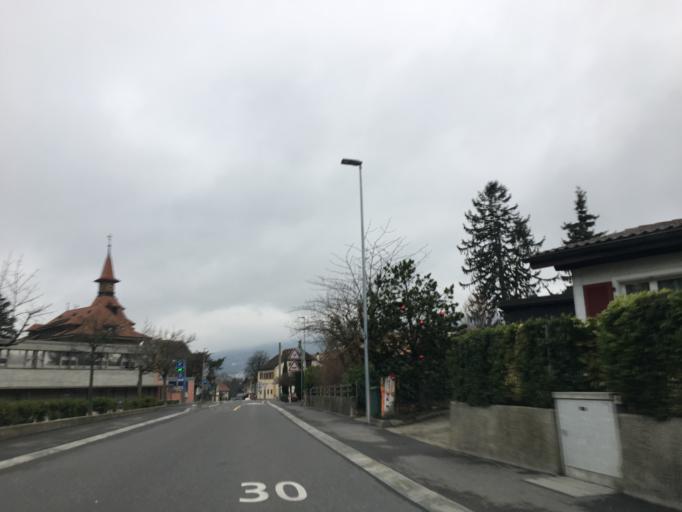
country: CH
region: Neuchatel
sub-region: Neuchatel District
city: Saint-Blaise
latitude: 47.0093
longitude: 7.0033
